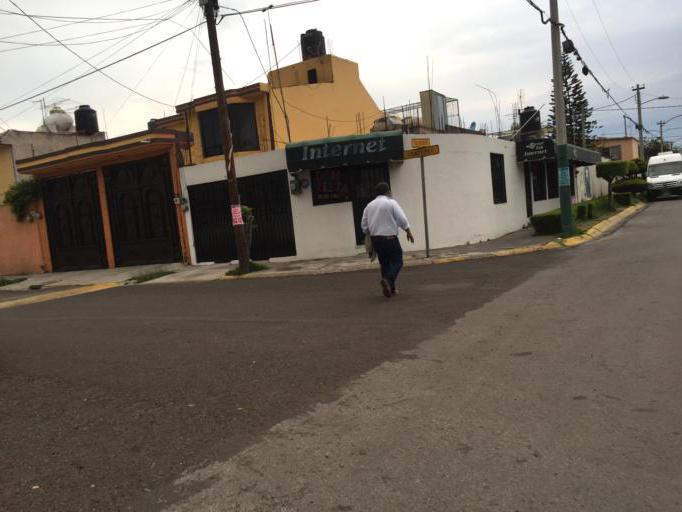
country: MX
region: Mexico
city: Cuautitlan Izcalli
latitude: 19.6551
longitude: -99.2106
